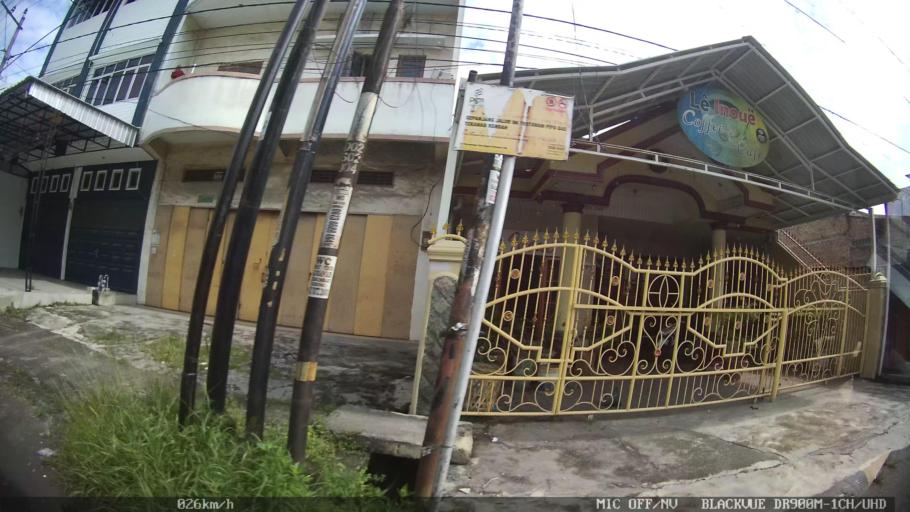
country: ID
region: North Sumatra
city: Medan
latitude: 3.6103
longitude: 98.6406
